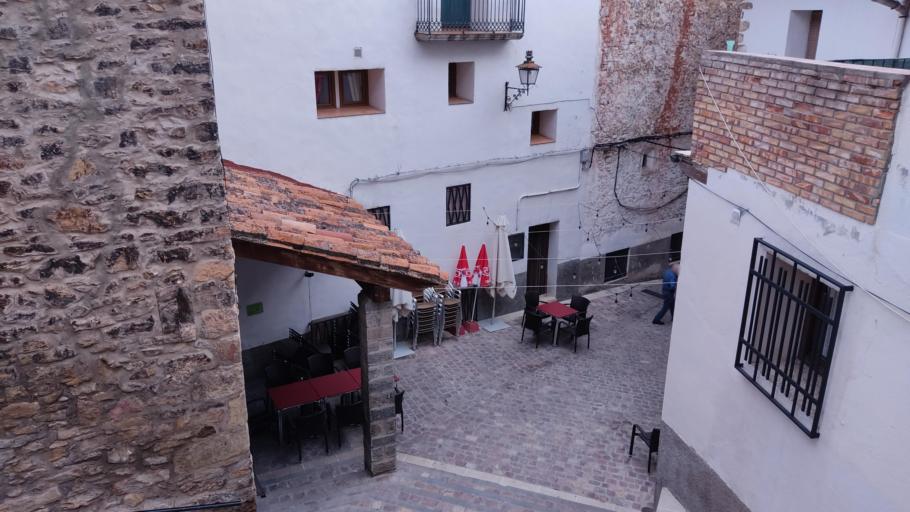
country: ES
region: Aragon
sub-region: Provincia de Teruel
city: Linares de Mora
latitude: 40.3215
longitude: -0.5750
